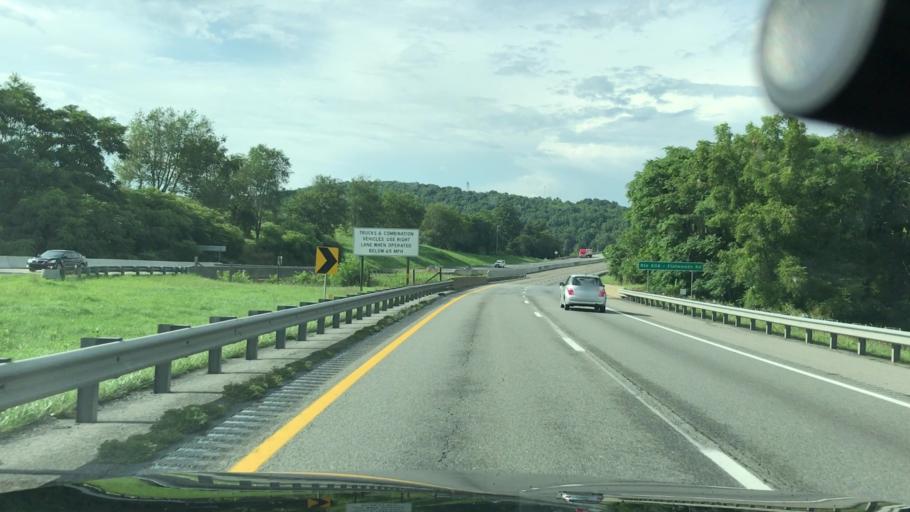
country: US
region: Virginia
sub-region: Carroll County
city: Woodlawn
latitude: 36.8668
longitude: -80.8719
